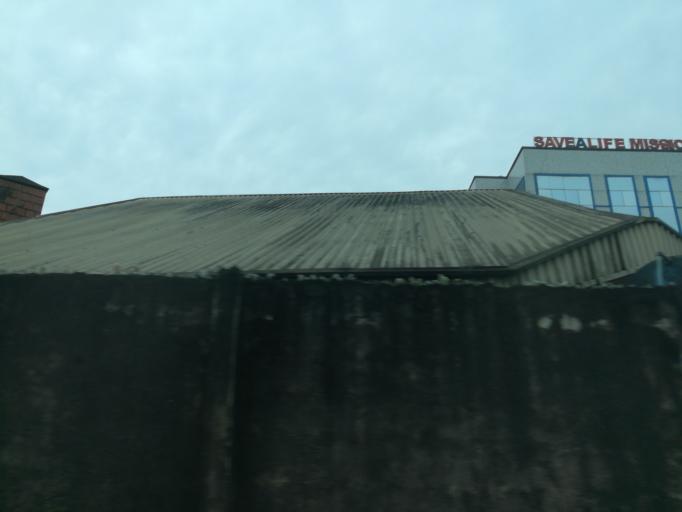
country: NG
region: Rivers
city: Port Harcourt
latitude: 4.8293
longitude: 7.0193
